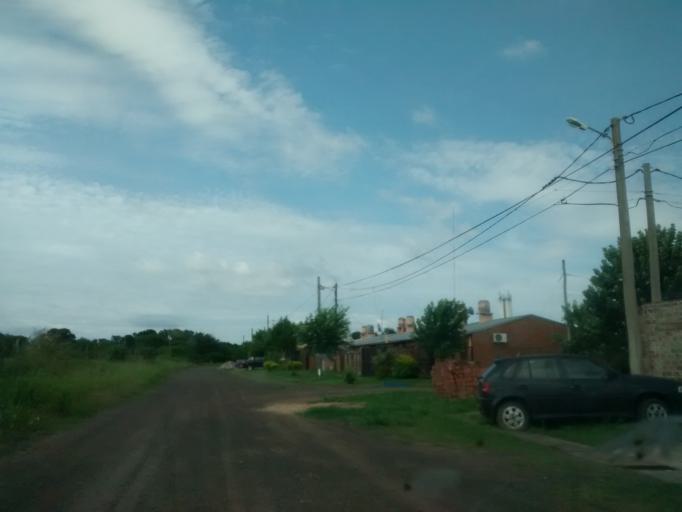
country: AR
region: Chaco
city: Resistencia
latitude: -27.4130
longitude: -58.9630
